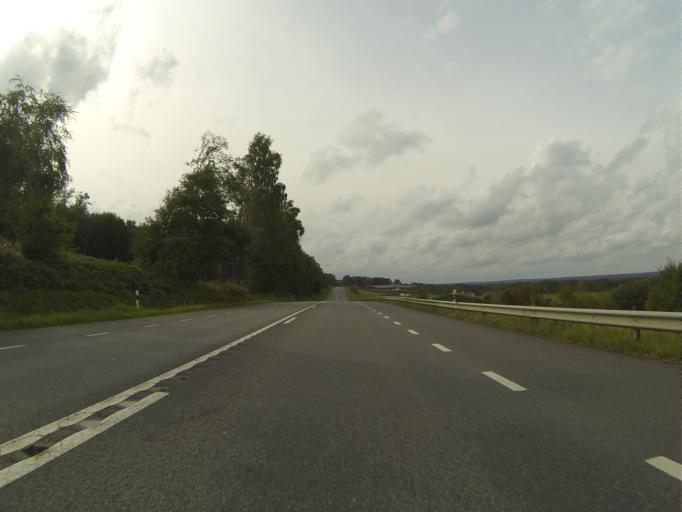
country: SE
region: Skane
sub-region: Kristianstads Kommun
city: Onnestad
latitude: 55.9340
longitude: 13.9197
